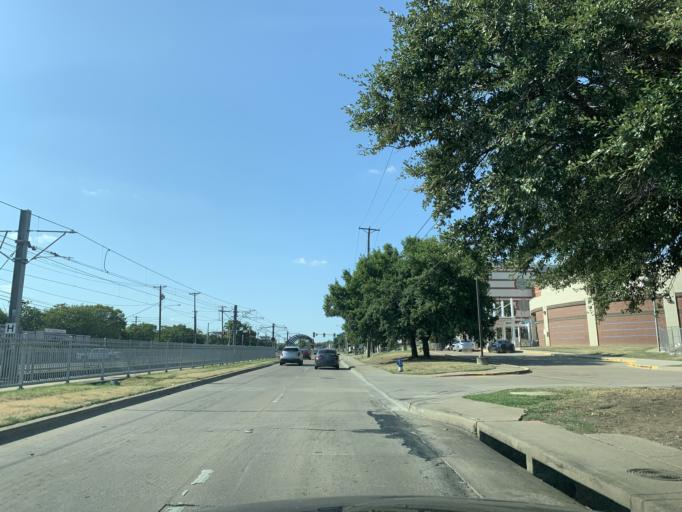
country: US
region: Texas
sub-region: Dallas County
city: Hutchins
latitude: 32.6906
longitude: -96.7915
